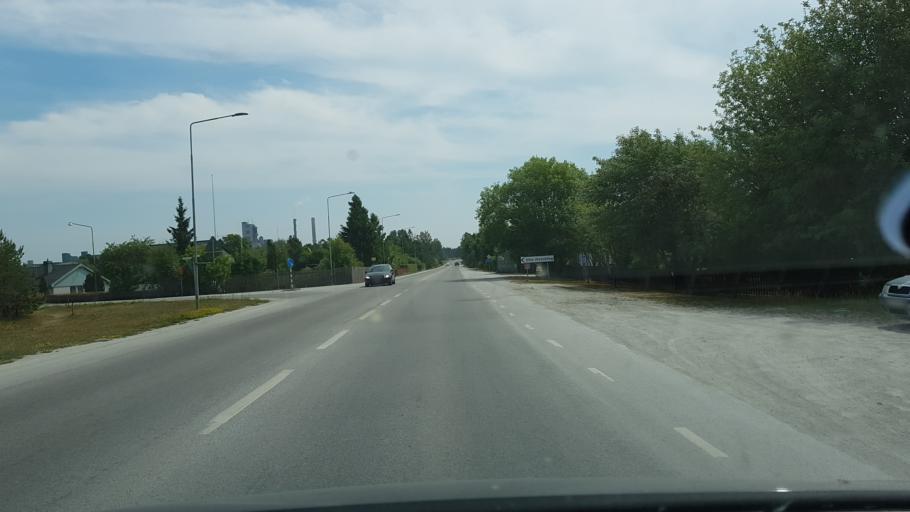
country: SE
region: Gotland
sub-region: Gotland
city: Slite
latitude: 57.7207
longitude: 18.7903
